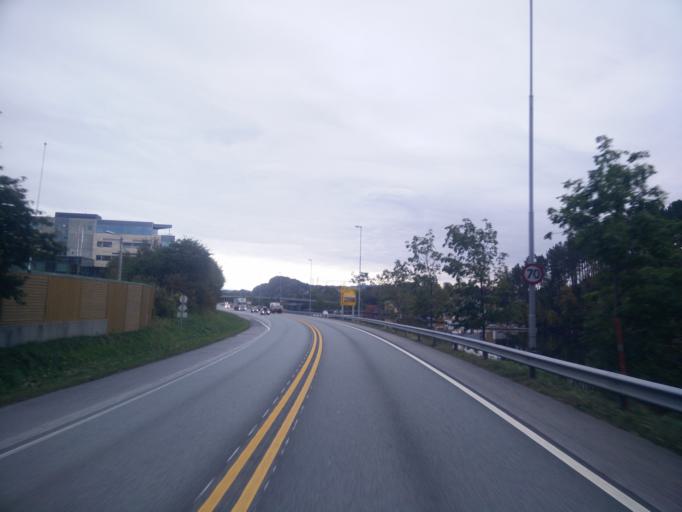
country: NO
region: More og Romsdal
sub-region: Sula
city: Langevag
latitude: 62.4703
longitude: 6.2310
